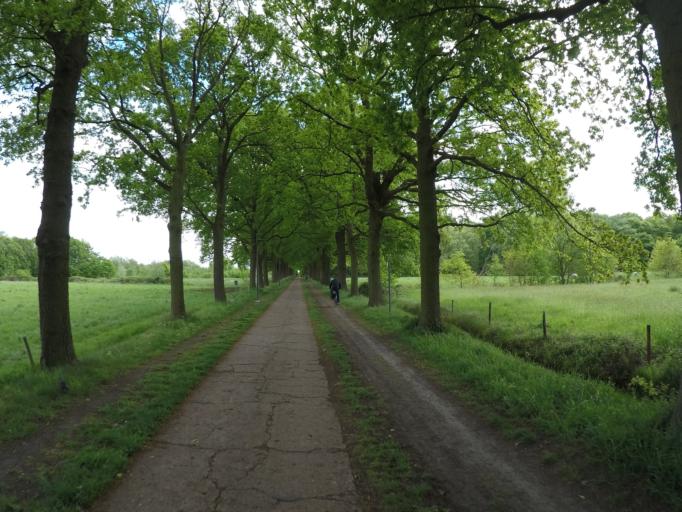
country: BE
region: Flanders
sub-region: Provincie Antwerpen
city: Hoboken
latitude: 51.1560
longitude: 4.3604
